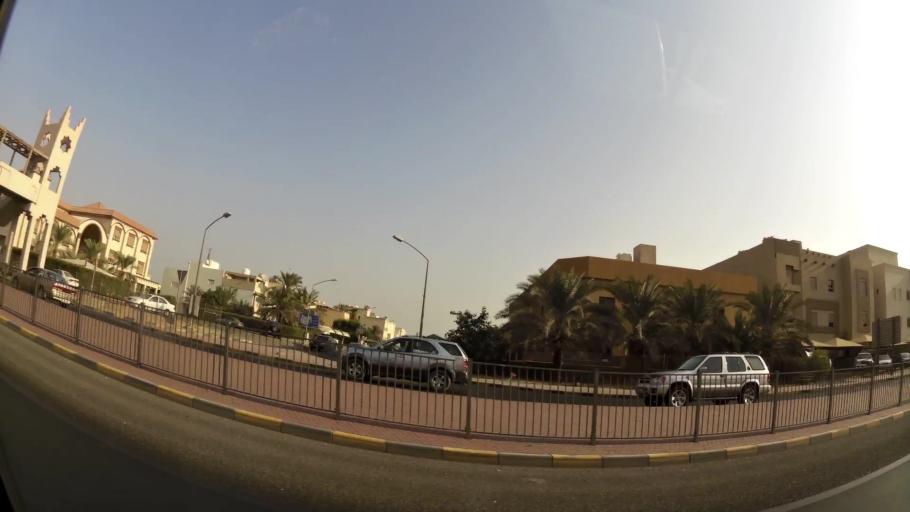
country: KW
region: Muhafazat Hawalli
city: Ar Rumaythiyah
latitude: 29.3205
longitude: 48.0616
